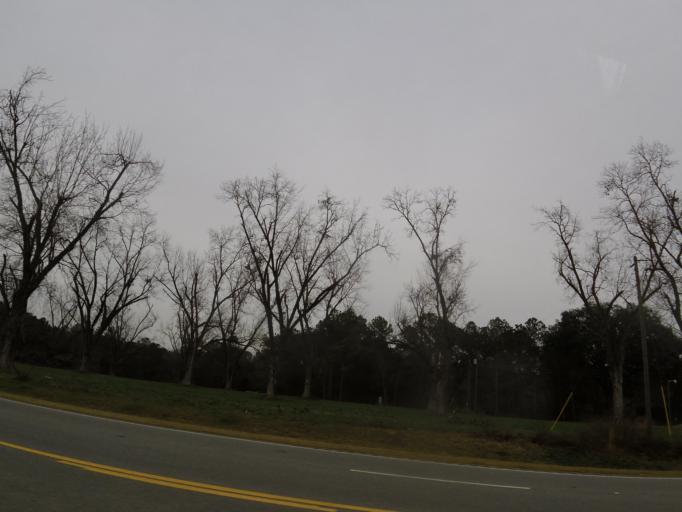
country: US
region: Georgia
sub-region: Grady County
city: Cairo
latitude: 30.8703
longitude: -84.1532
